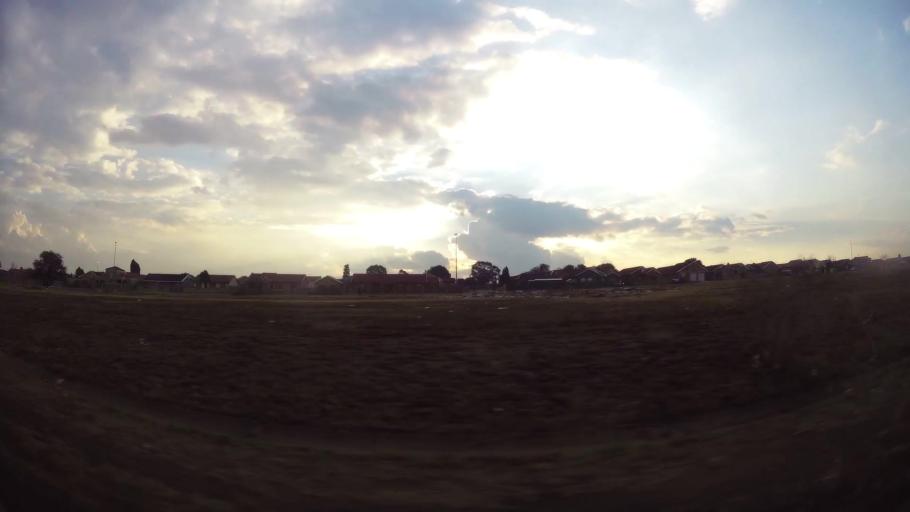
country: ZA
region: Gauteng
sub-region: City of Johannesburg Metropolitan Municipality
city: Orange Farm
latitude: -26.5862
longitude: 27.8539
